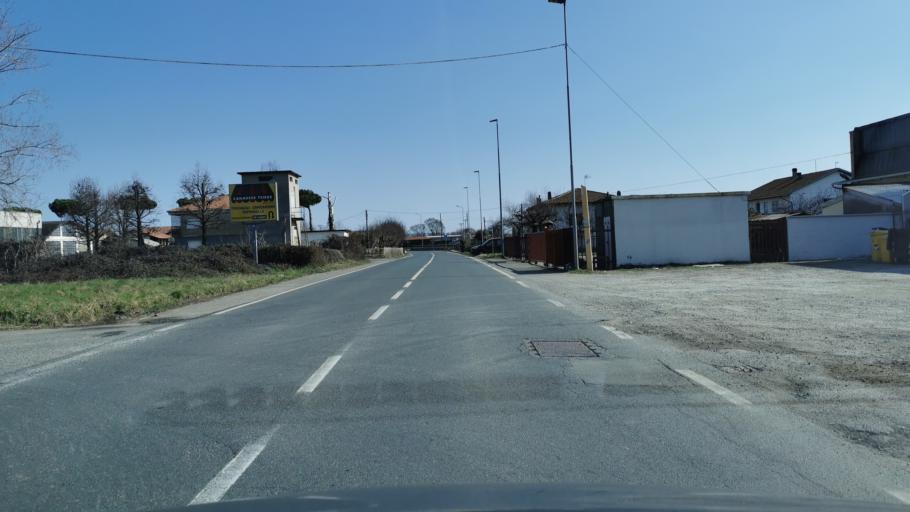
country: IT
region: Piedmont
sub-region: Provincia di Torino
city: Busano
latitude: 45.3289
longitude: 7.6695
